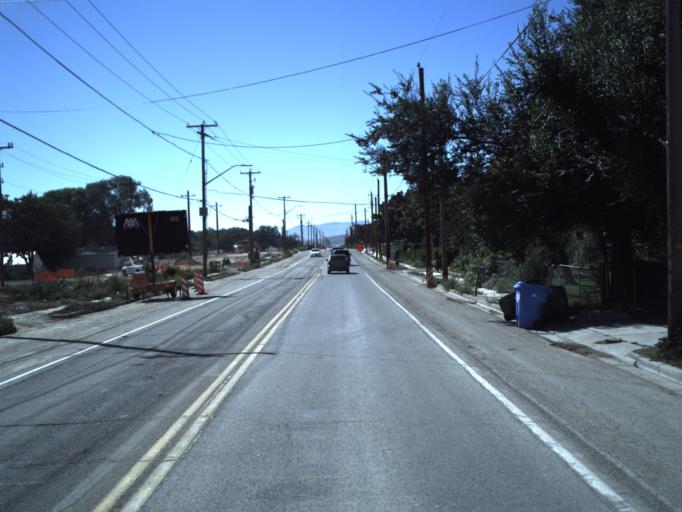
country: US
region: Utah
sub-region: Salt Lake County
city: Riverton
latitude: 40.5161
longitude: -111.9388
